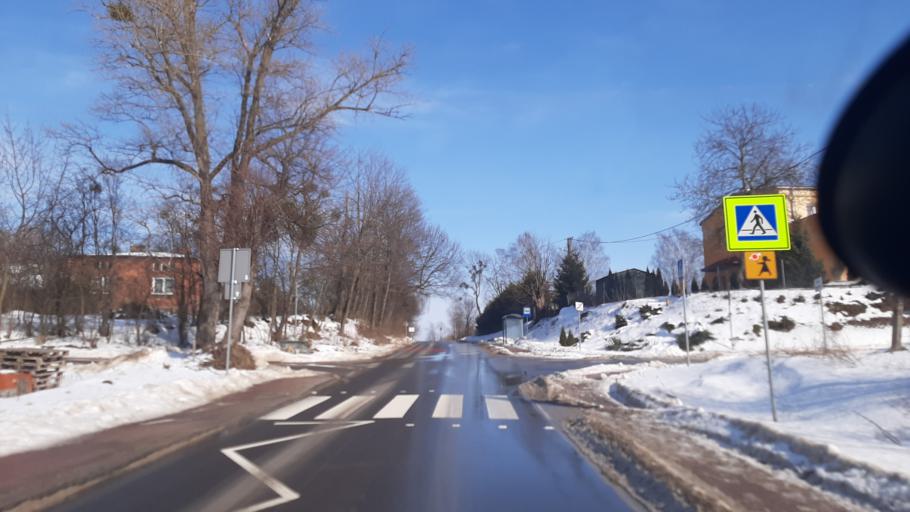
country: PL
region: Lublin Voivodeship
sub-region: Powiat pulawski
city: Kurow
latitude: 51.3589
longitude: 22.1352
